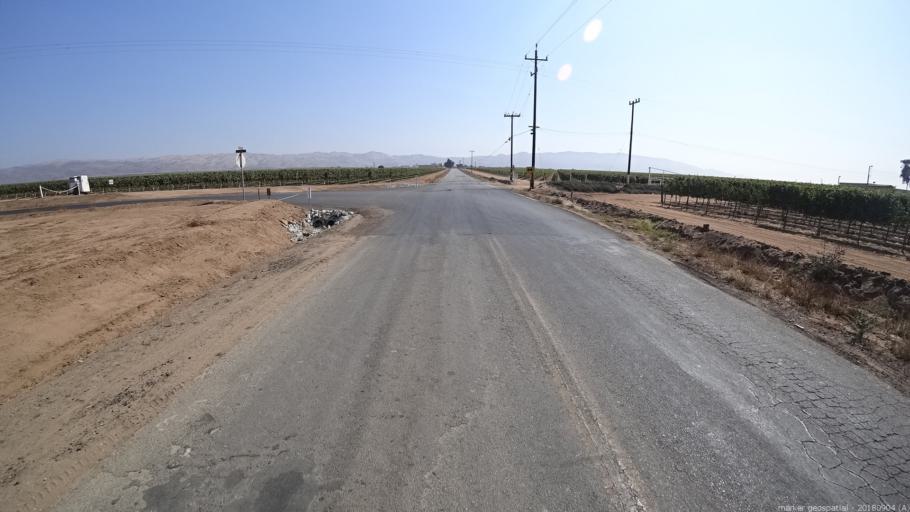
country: US
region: California
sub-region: Monterey County
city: Gonzales
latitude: 36.5015
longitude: -121.3955
